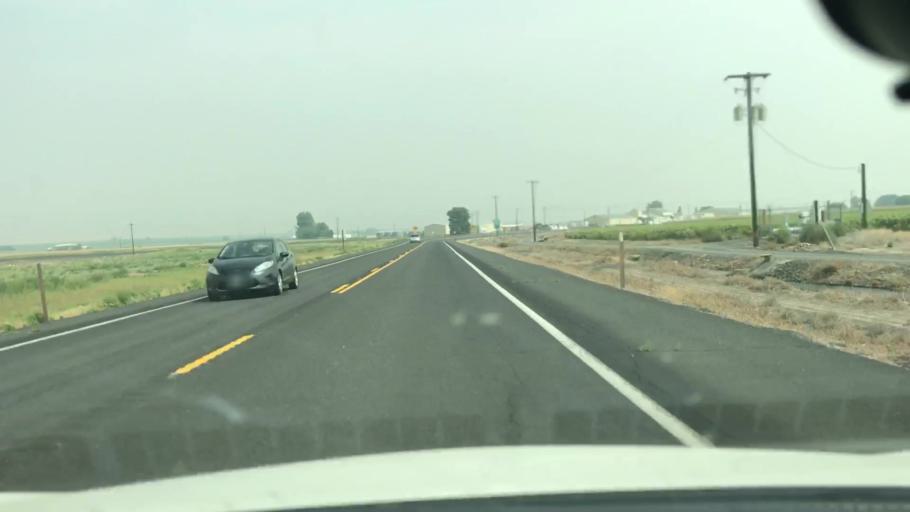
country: US
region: Washington
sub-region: Grant County
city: Quincy
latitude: 47.2465
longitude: -119.7297
